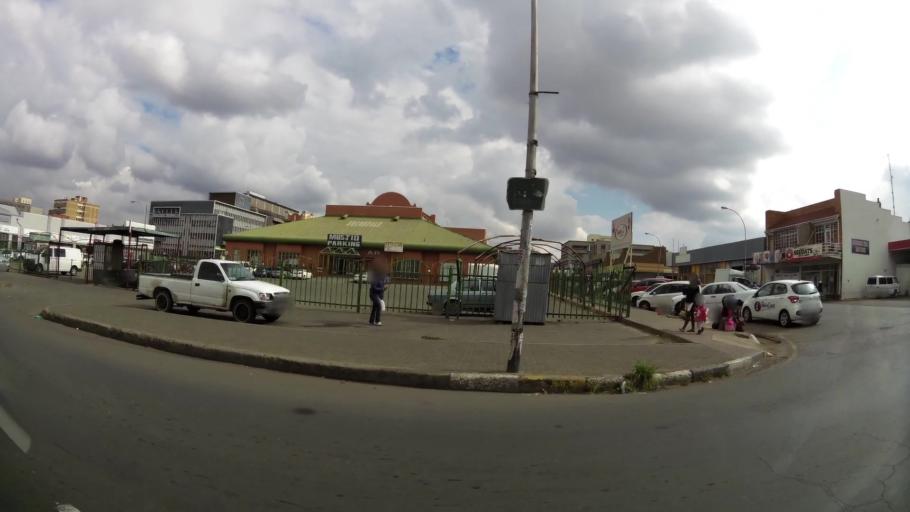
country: ZA
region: Orange Free State
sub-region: Mangaung Metropolitan Municipality
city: Bloemfontein
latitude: -29.1162
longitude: 26.2255
